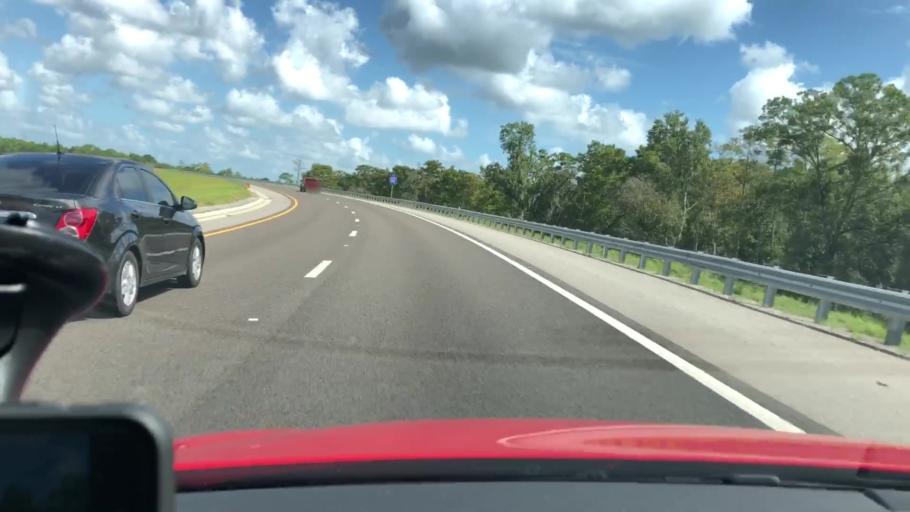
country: US
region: Florida
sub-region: Volusia County
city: Samsula-Spruce Creek
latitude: 29.1338
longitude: -81.1198
